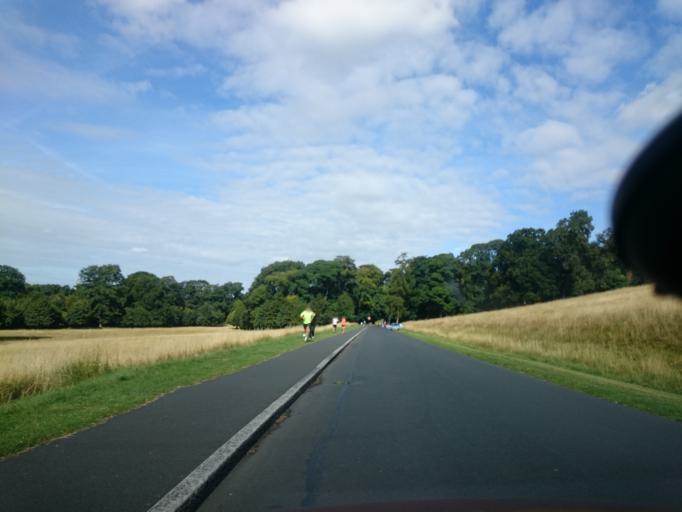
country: IE
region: Leinster
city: Chapelizod
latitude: 53.3474
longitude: -6.3310
